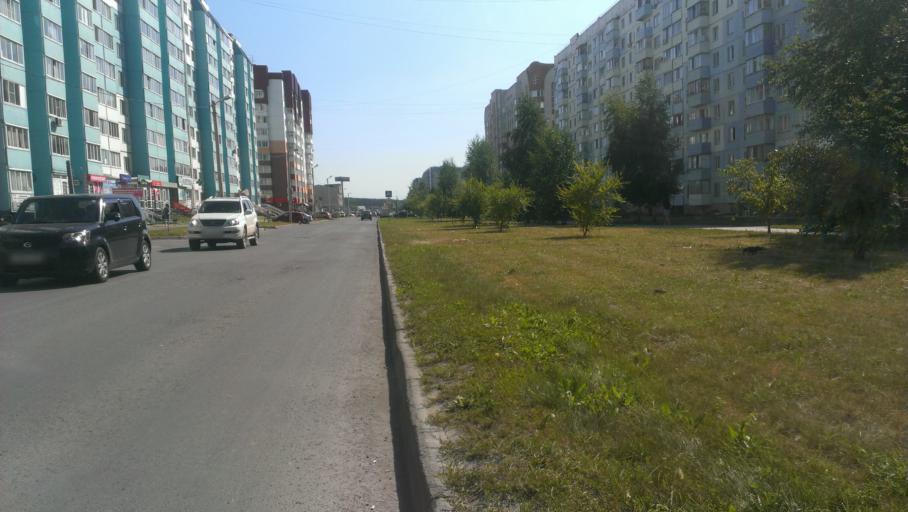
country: RU
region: Altai Krai
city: Novosilikatnyy
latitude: 53.3326
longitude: 83.6849
